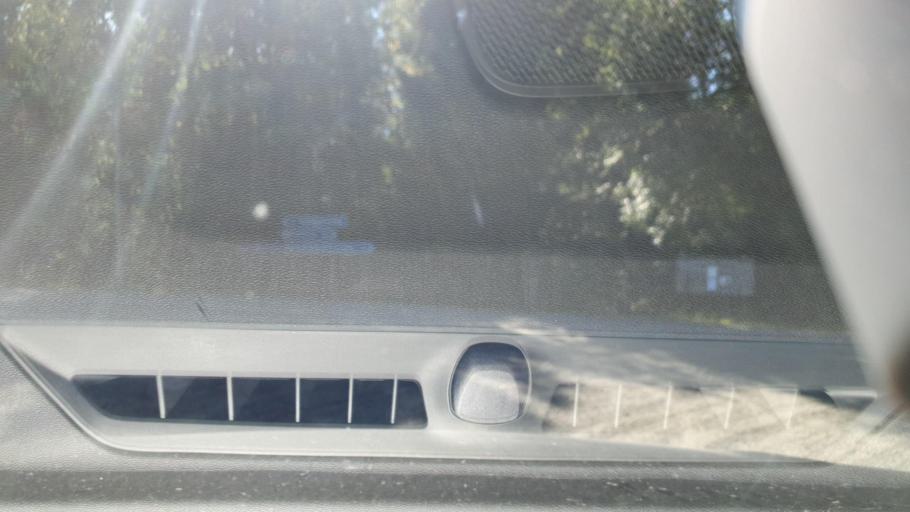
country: SE
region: Vaermland
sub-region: Filipstads Kommun
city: Lesjofors
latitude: 59.9063
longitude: 14.1017
